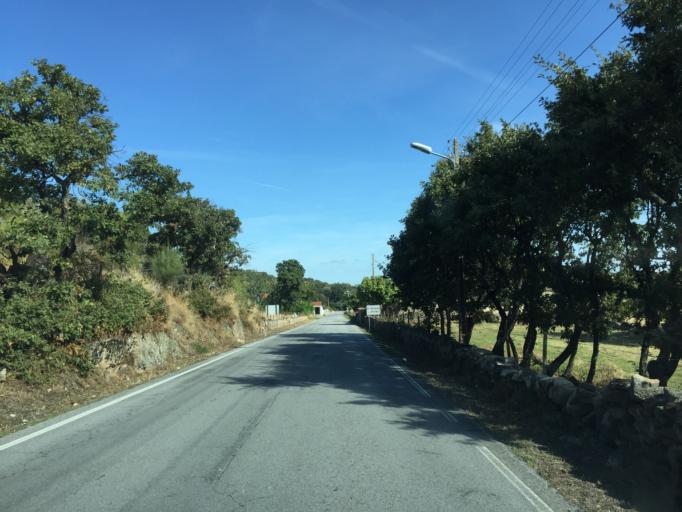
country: PT
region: Portalegre
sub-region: Marvao
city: Marvao
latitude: 39.4070
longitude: -7.3564
